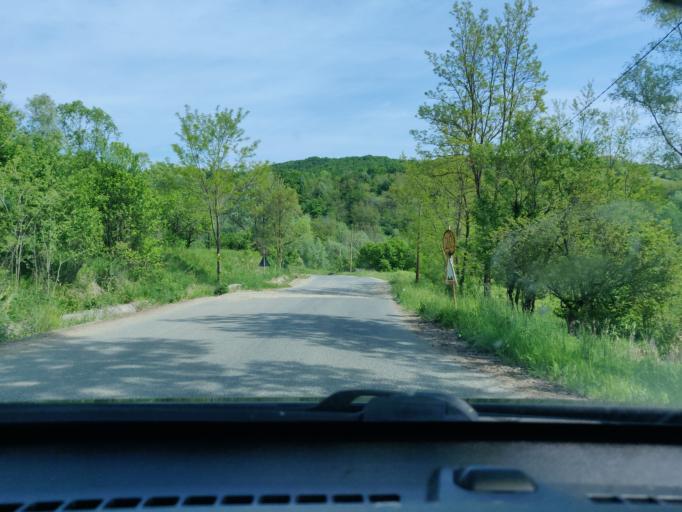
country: RO
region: Vrancea
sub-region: Comuna Vidra
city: Vidra
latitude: 45.9231
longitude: 26.8954
